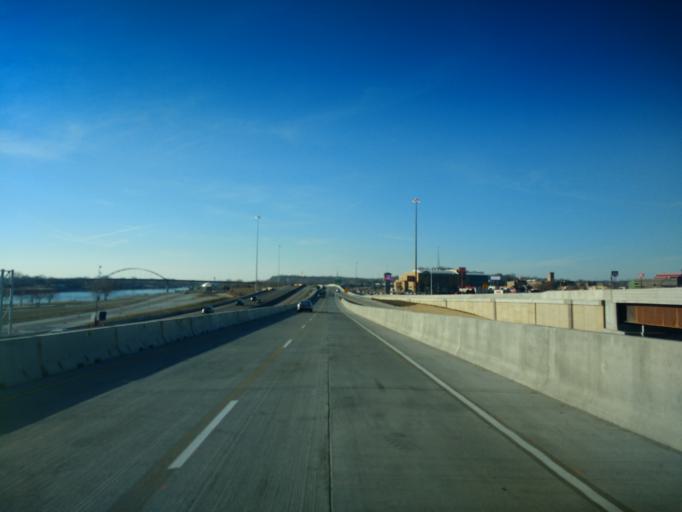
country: US
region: Iowa
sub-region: Woodbury County
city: Sioux City
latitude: 42.4885
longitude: -96.3991
